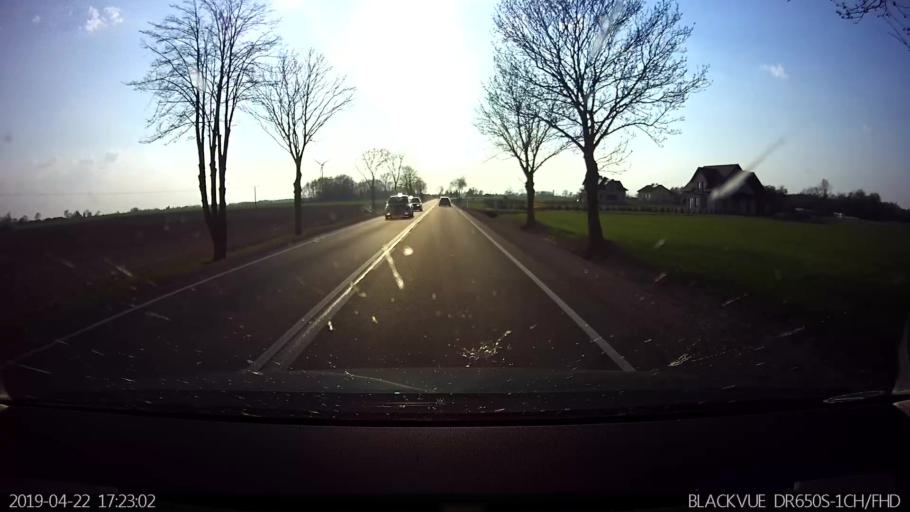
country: PL
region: Masovian Voivodeship
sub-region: Powiat sokolowski
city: Repki
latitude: 52.3897
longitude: 22.3262
